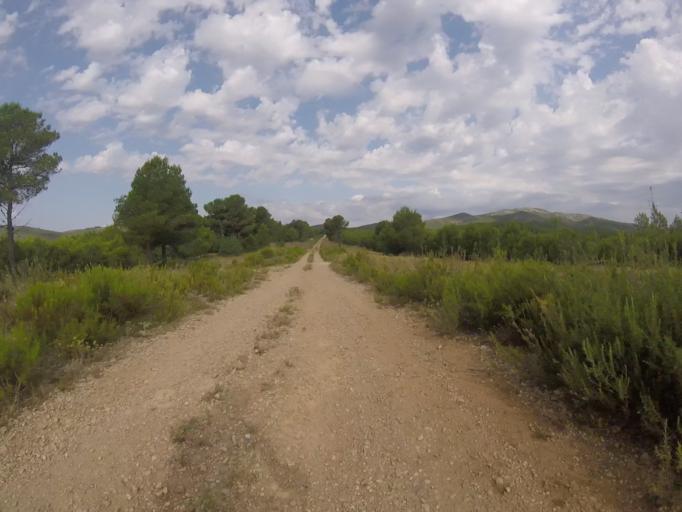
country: ES
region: Valencia
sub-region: Provincia de Castello
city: Alcala de Xivert
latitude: 40.3620
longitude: 0.2005
